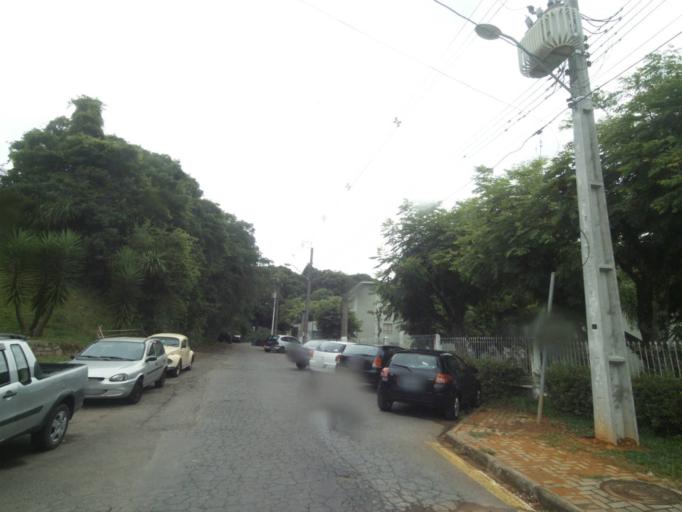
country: BR
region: Parana
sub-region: Curitiba
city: Curitiba
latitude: -25.4623
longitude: -49.3374
